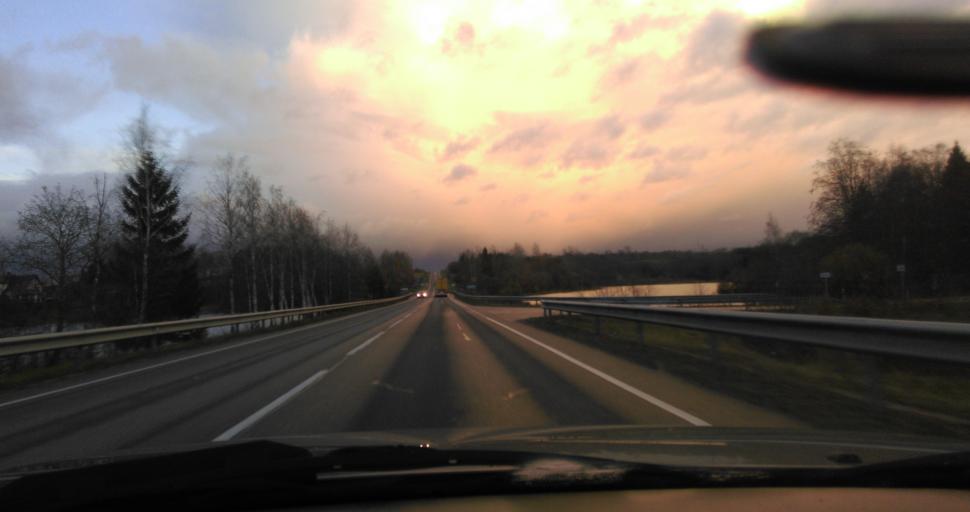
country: LT
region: Utenos apskritis
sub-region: Utena
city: Utena
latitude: 55.5155
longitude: 25.6508
